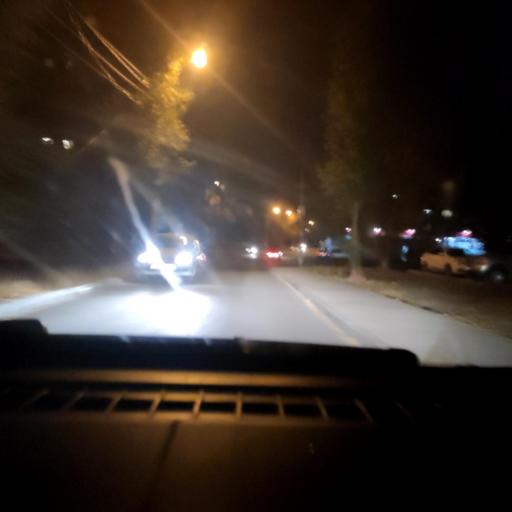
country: RU
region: Voronezj
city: Voronezh
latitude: 51.7206
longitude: 39.2642
